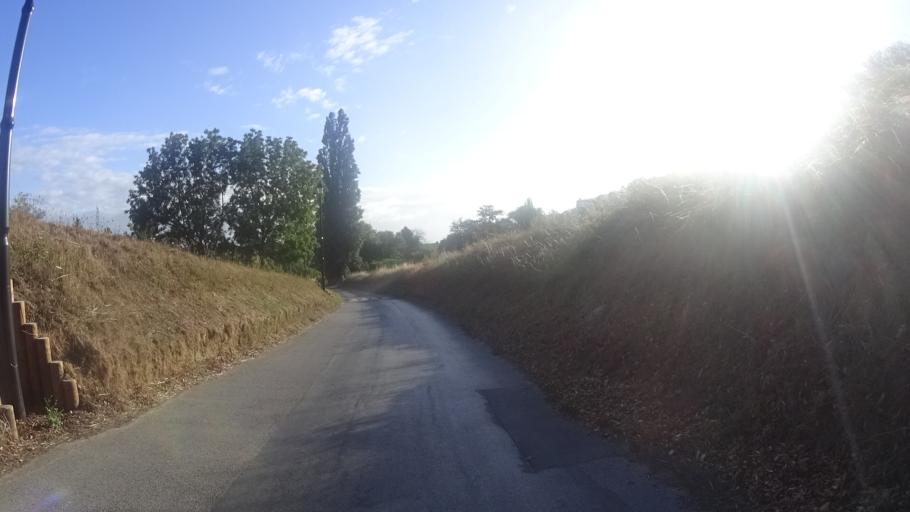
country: FR
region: Picardie
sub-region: Departement de l'Oise
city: Verberie
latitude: 49.3056
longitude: 2.6953
